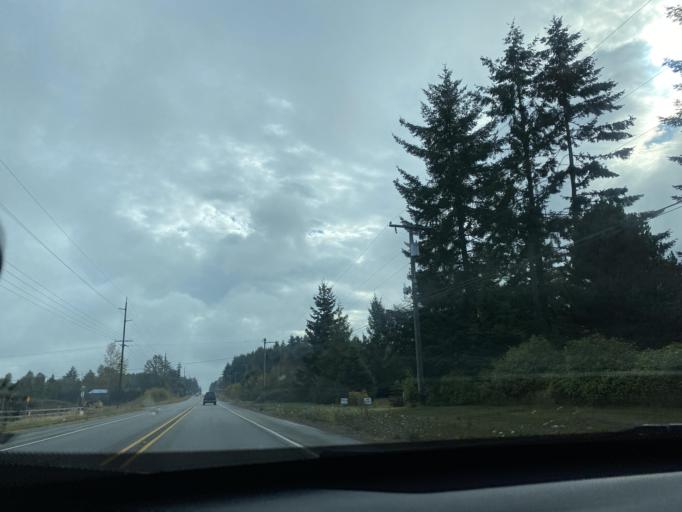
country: US
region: Washington
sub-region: Clallam County
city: Port Angeles
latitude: 48.1032
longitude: -123.4991
